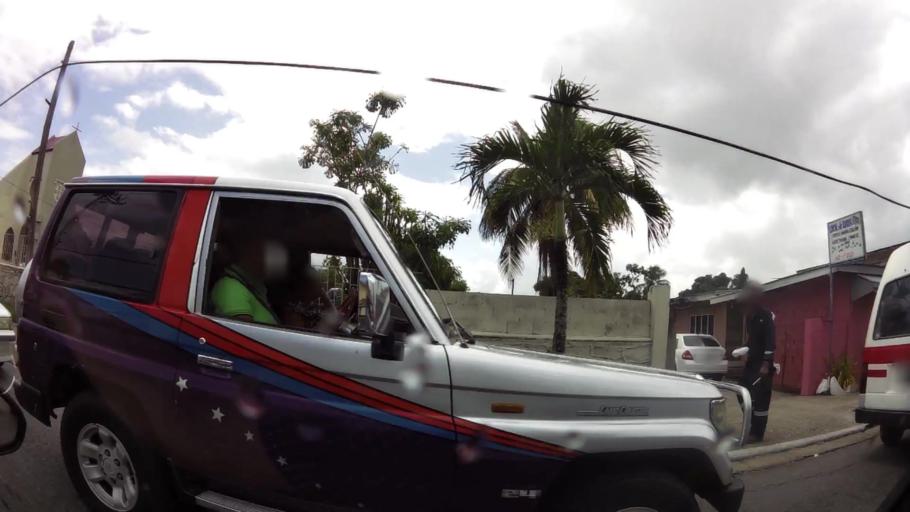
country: TT
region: Tunapuna/Piarco
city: Arouca
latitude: 10.6338
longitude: -61.3358
